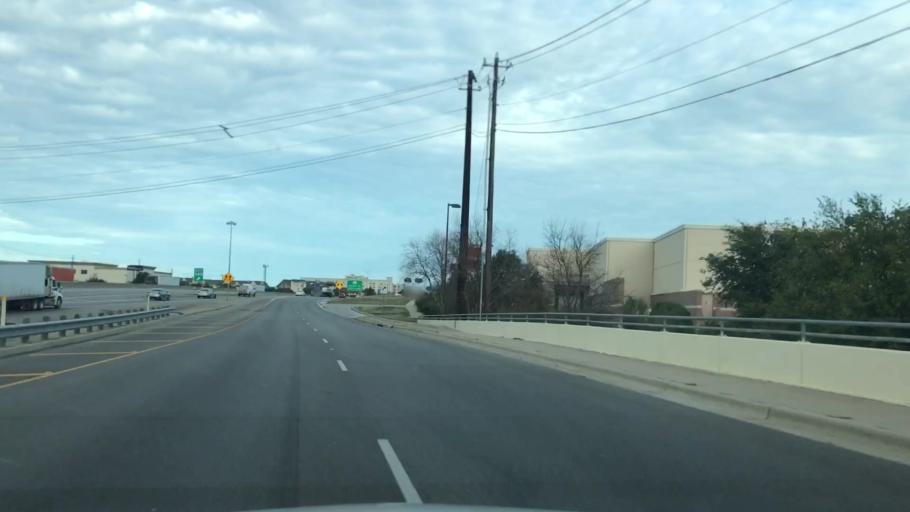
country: US
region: Texas
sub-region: Travis County
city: Wells Branch
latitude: 30.4004
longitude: -97.6735
